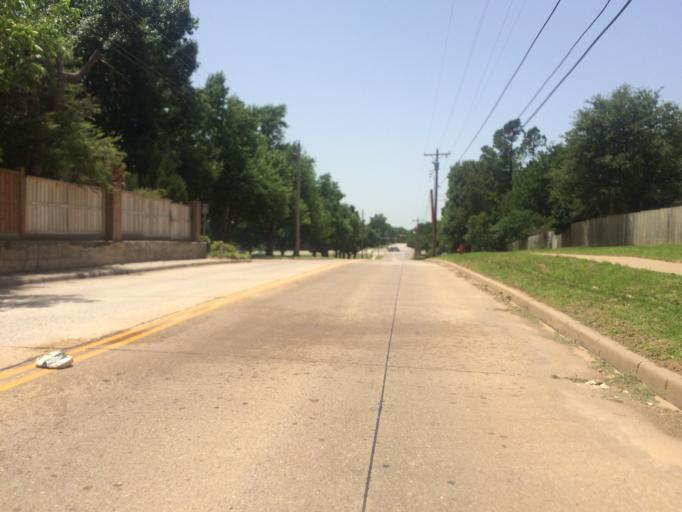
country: US
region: Oklahoma
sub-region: Cleveland County
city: Norman
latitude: 35.1894
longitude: -97.4617
